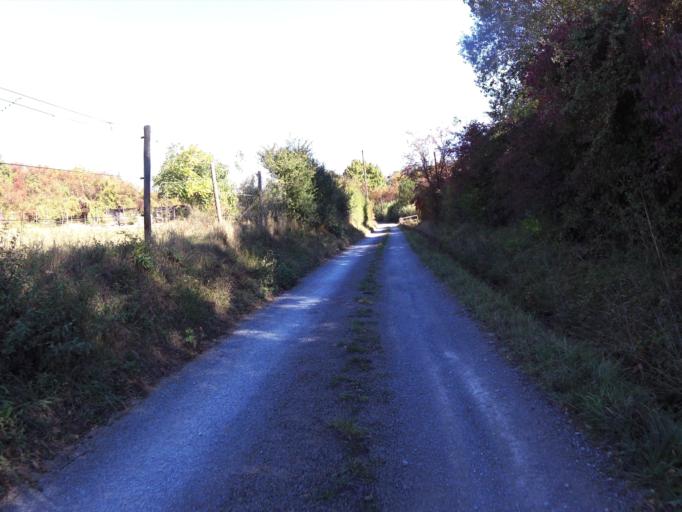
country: DE
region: Bavaria
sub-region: Regierungsbezirk Unterfranken
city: Reichenberg
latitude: 49.7544
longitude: 9.9401
